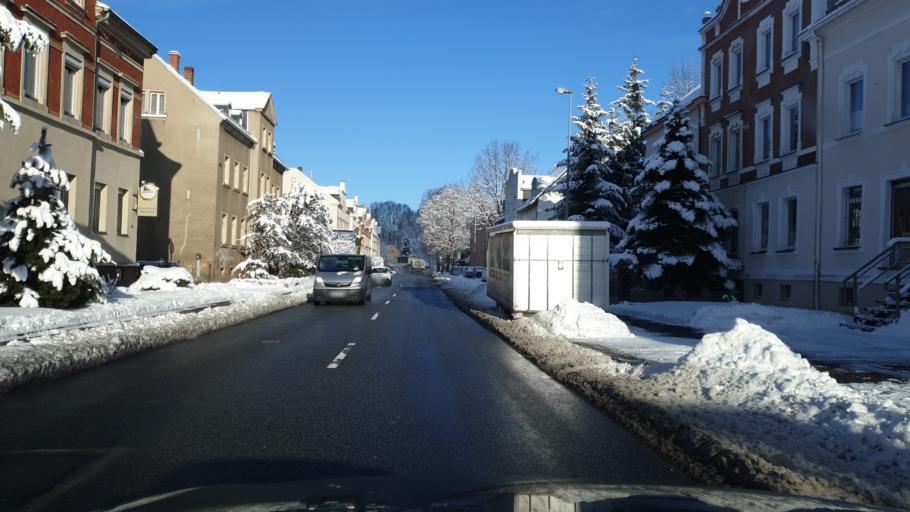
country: DE
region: Saxony
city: Chemnitz
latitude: 50.8646
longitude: 12.9194
